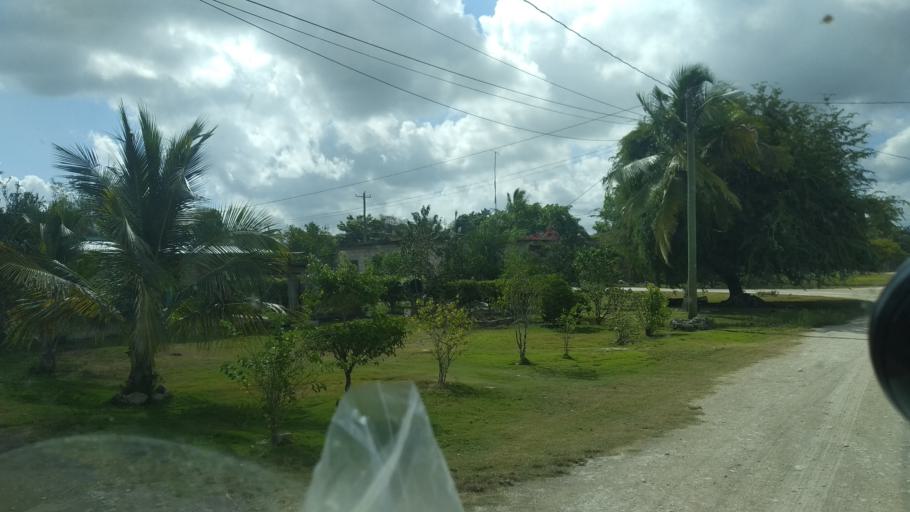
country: BZ
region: Corozal
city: Corozal
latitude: 18.3501
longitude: -88.4990
